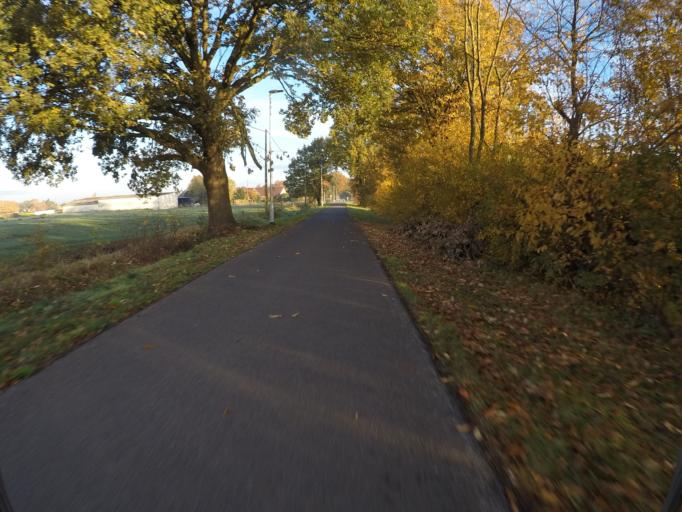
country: BE
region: Flanders
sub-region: Provincie Antwerpen
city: Olen
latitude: 51.1129
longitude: 4.8255
